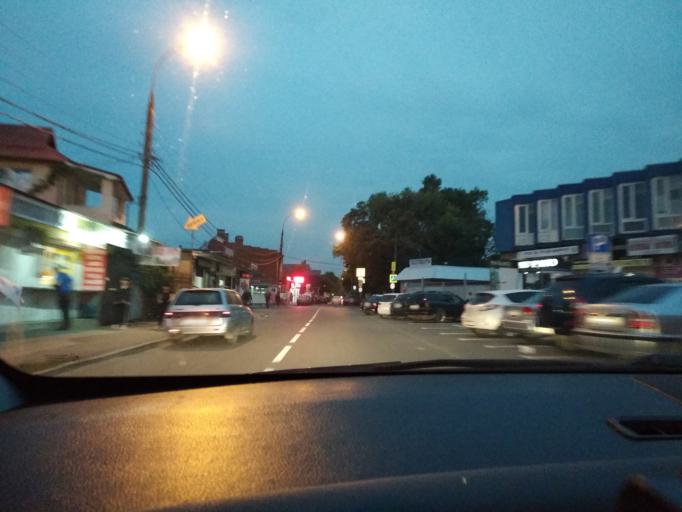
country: RU
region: Krasnodarskiy
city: Krasnodar
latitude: 45.0191
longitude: 38.9993
